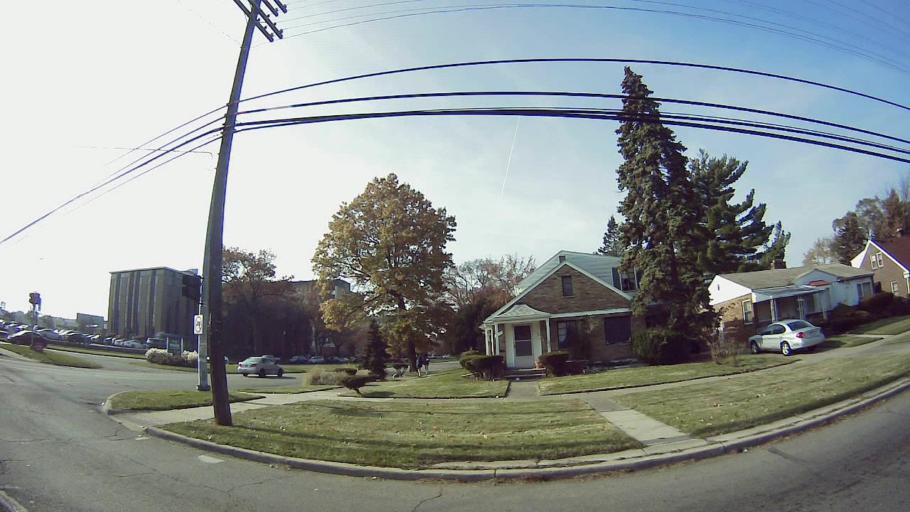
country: US
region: Michigan
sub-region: Oakland County
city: Oak Park
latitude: 42.4207
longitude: -83.1801
